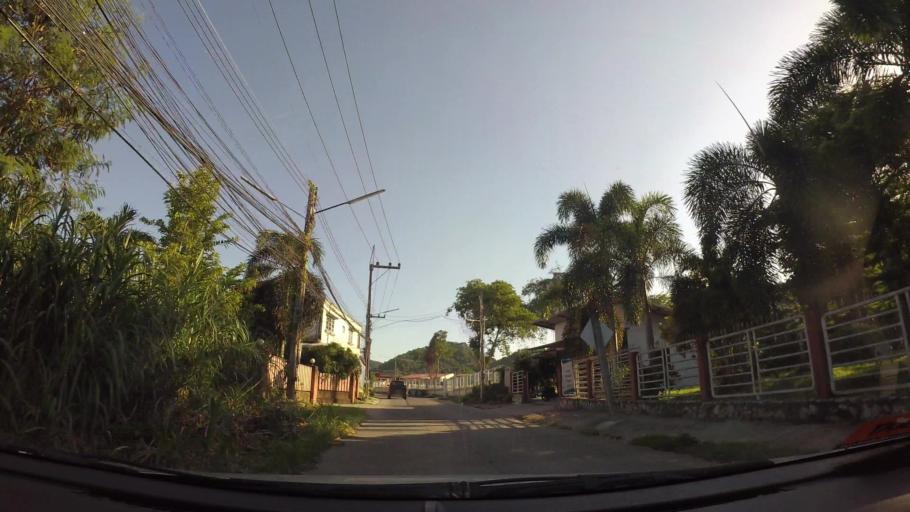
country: TH
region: Chon Buri
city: Si Racha
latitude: 13.1494
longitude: 100.9325
